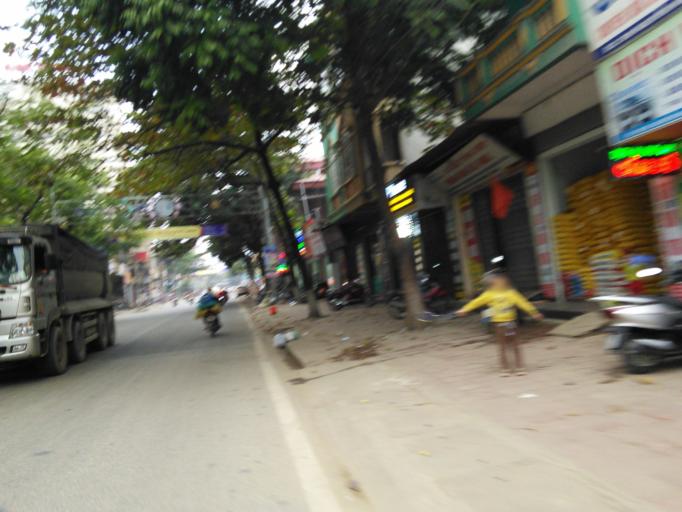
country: VN
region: Lao Cai
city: Lao Cai
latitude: 22.4901
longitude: 103.9785
